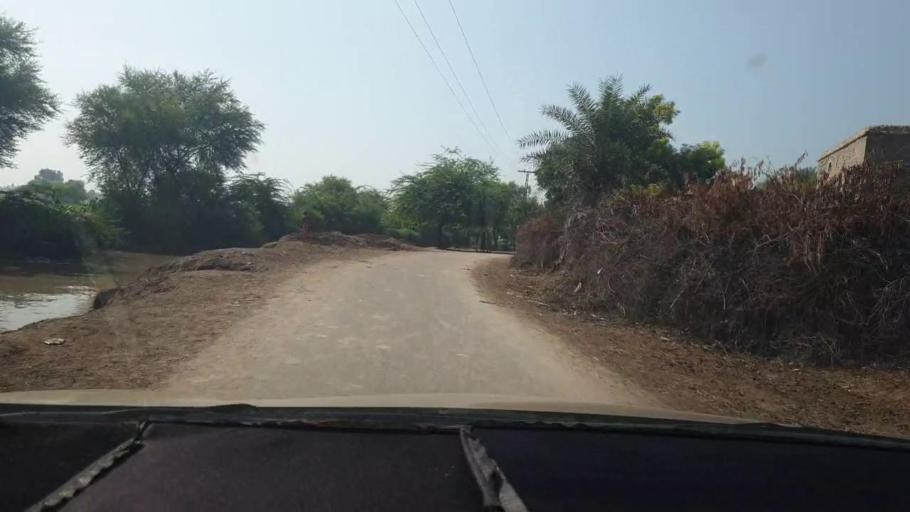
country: PK
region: Sindh
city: Kambar
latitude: 27.5768
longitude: 68.0751
